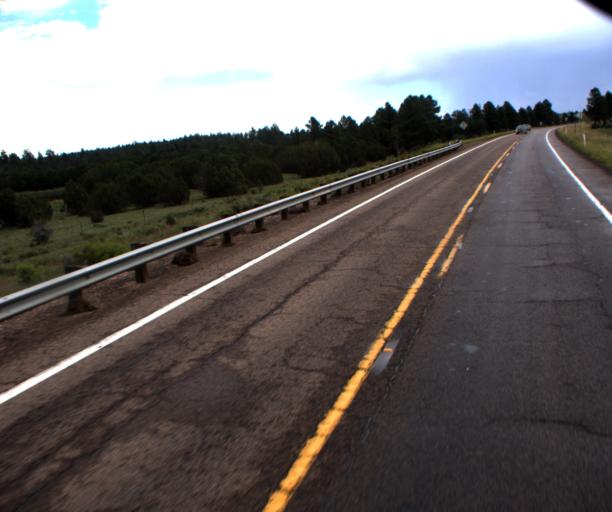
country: US
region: Arizona
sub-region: Navajo County
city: Heber-Overgaard
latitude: 34.3935
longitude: -110.5225
